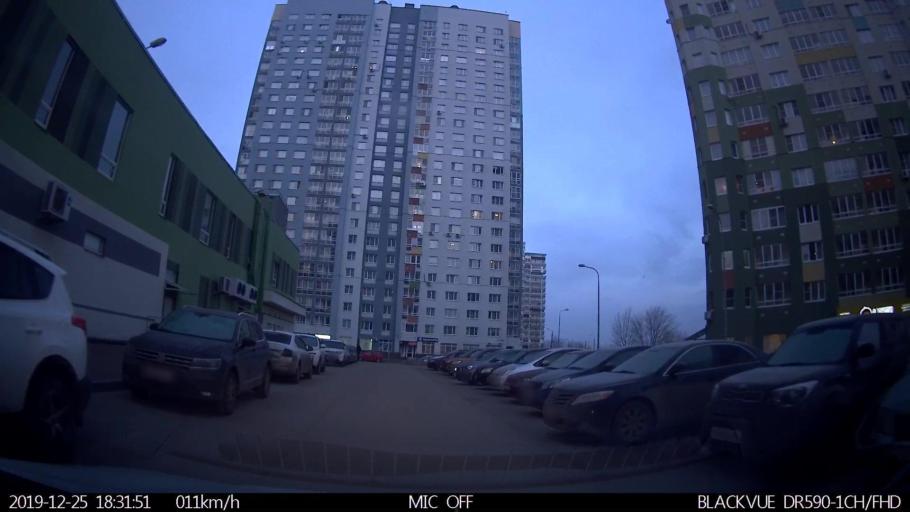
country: RU
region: Nizjnij Novgorod
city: Nizhniy Novgorod
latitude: 56.3422
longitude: 43.9470
